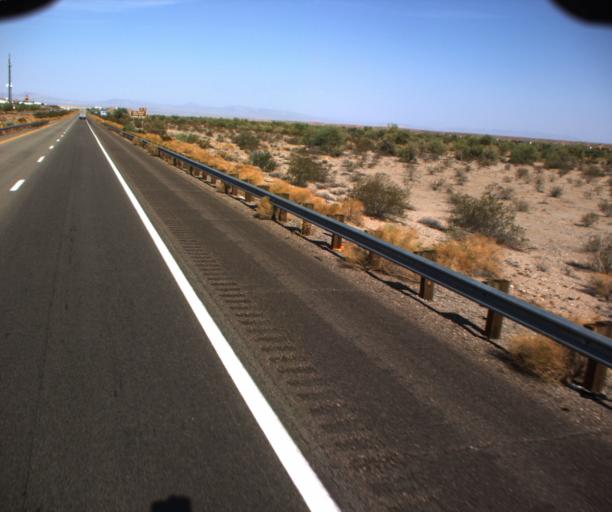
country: US
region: Arizona
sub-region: Mohave County
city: Desert Hills
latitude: 34.7302
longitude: -114.3000
